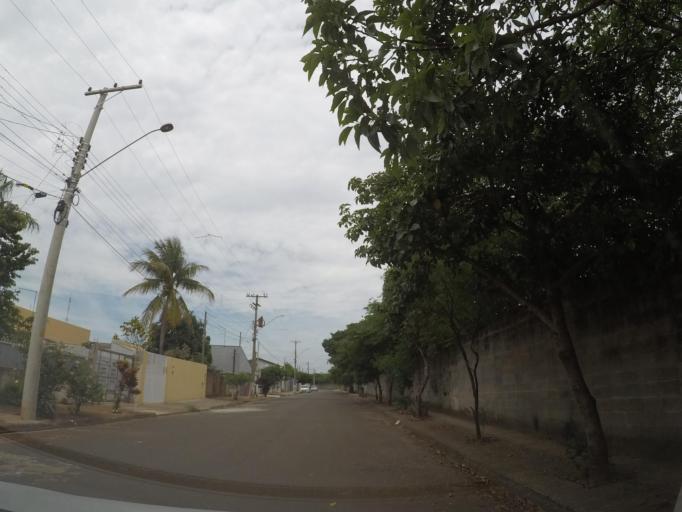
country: BR
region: Sao Paulo
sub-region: Hortolandia
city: Hortolandia
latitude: -22.8336
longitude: -47.1916
